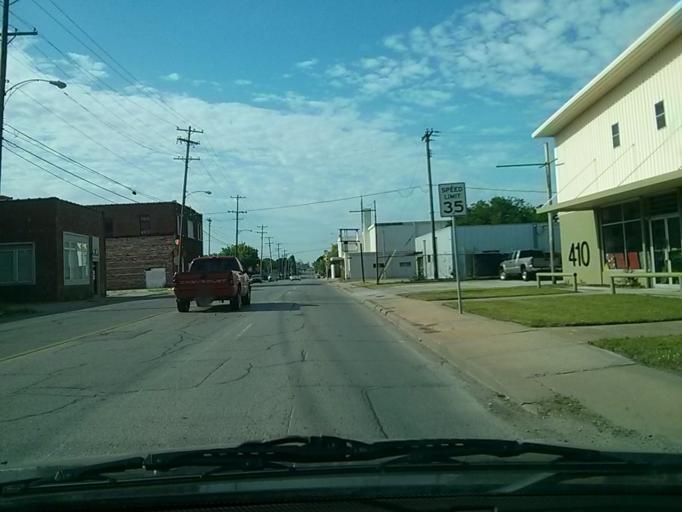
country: US
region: Oklahoma
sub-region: Tulsa County
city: Tulsa
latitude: 36.1556
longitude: -95.9757
